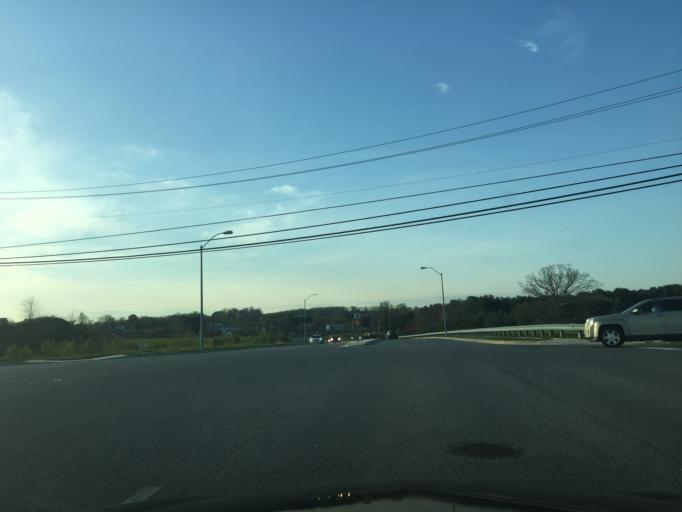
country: US
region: Maryland
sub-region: Baltimore County
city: Perry Hall
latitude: 39.4163
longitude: -76.4534
